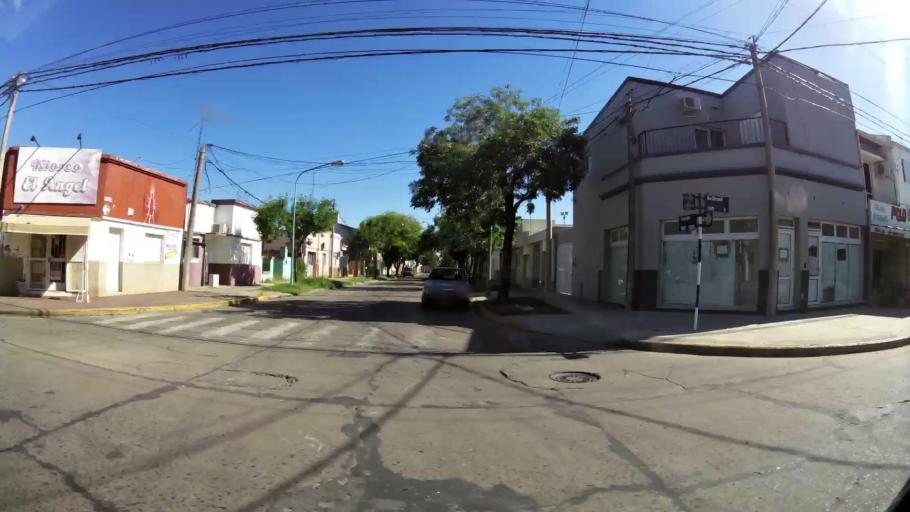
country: AR
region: Santa Fe
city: Rafaela
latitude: -31.2435
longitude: -61.4885
